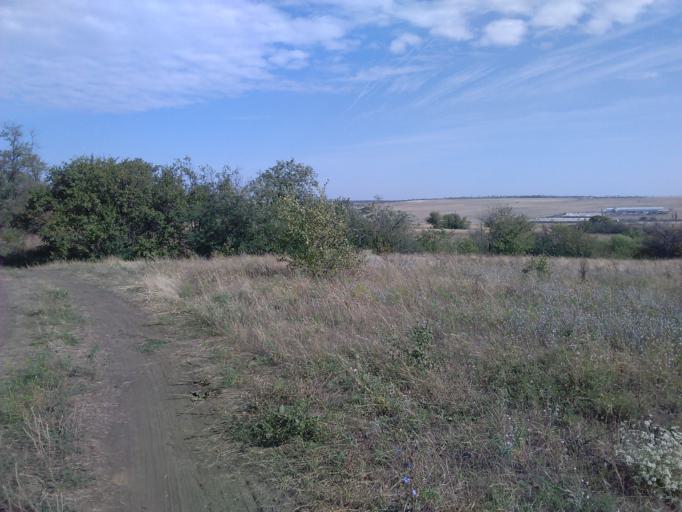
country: RU
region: Rostov
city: Gornyy
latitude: 47.8889
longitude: 40.2411
